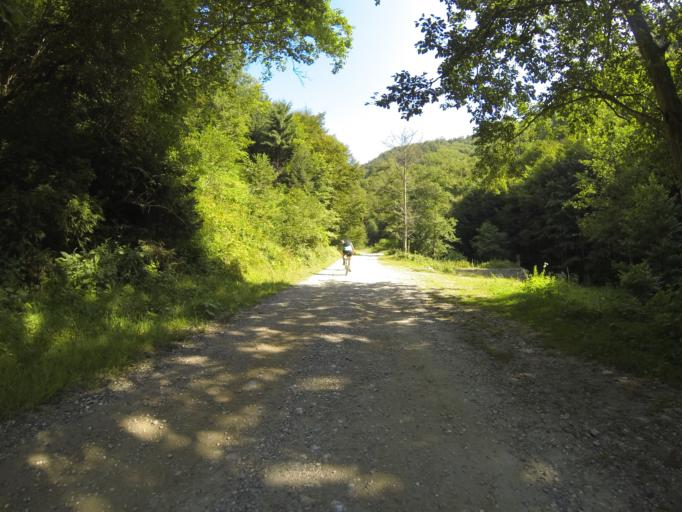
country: RO
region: Valcea
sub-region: Comuna Costesti
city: Bistrita
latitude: 45.2334
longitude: 24.0023
